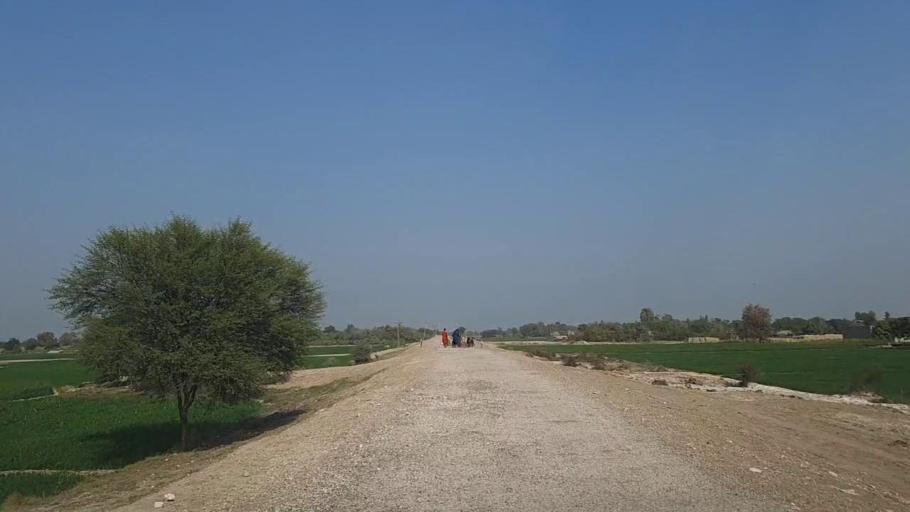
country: PK
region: Sindh
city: Moro
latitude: 26.7996
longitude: 67.9439
